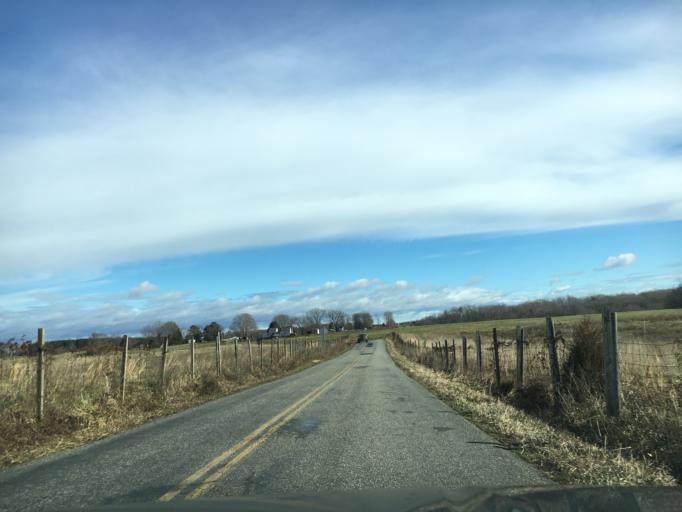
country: US
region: Virginia
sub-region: Amelia County
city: Amelia Court House
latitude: 37.4125
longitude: -78.0863
